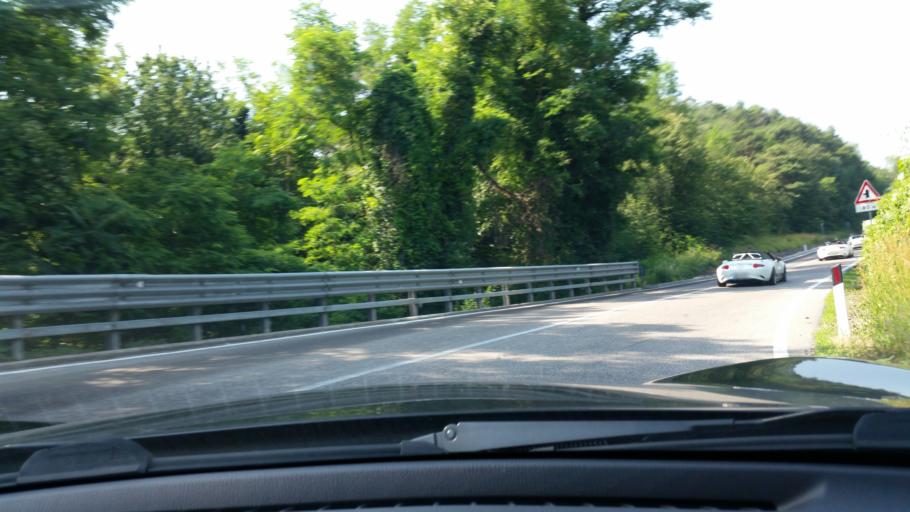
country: IT
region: Trentino-Alto Adige
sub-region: Bolzano
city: Ora
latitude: 46.3408
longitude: 11.2981
